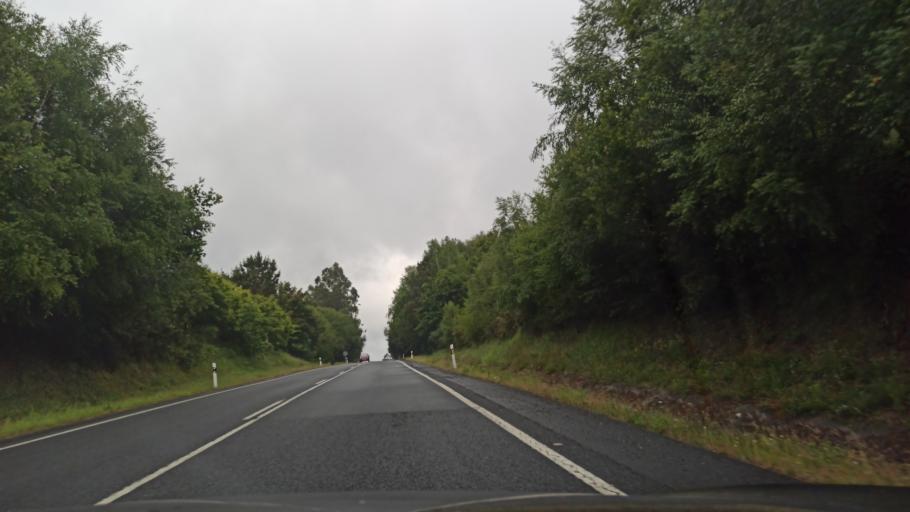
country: ES
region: Galicia
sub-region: Provincia da Coruna
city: Santiso
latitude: 42.7644
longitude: -8.0026
